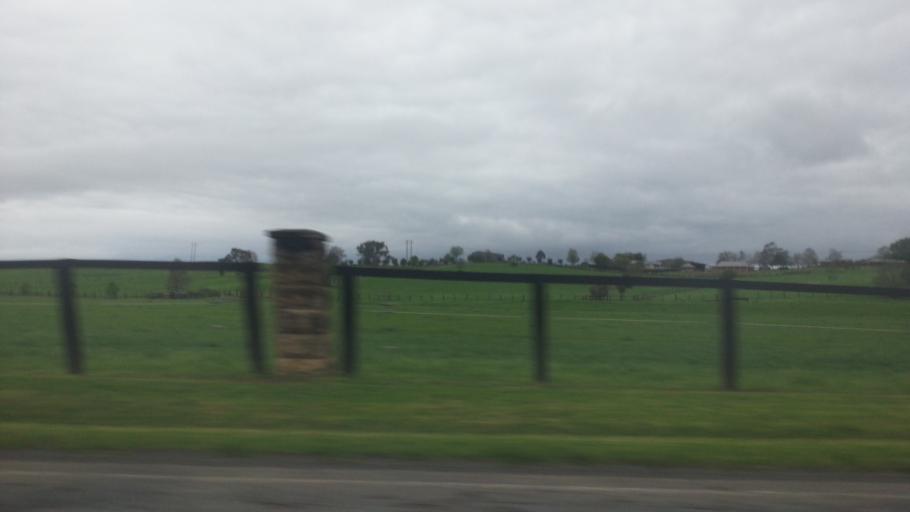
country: AU
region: New South Wales
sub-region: Wollondilly
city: Douglas Park
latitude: -34.1381
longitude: 150.7126
